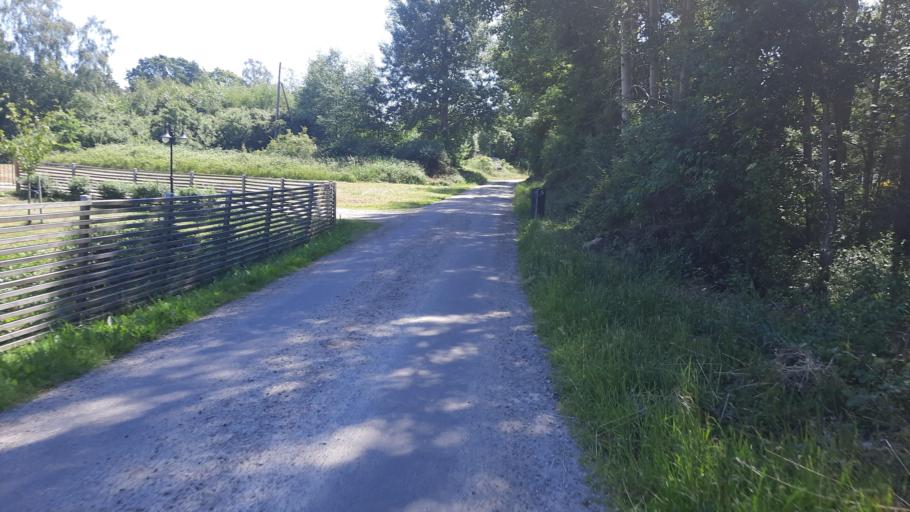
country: SE
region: Blekinge
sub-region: Karlskrona Kommun
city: Jaemjoe
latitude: 56.1509
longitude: 15.7573
